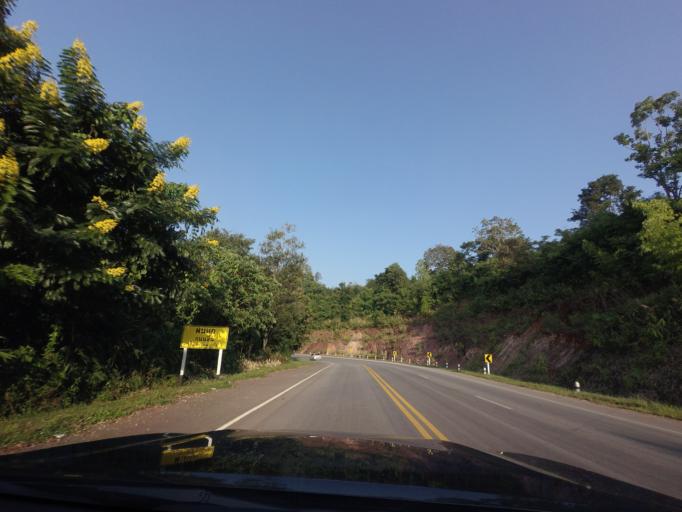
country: TH
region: Loei
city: Dan Sai
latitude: 17.2268
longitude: 101.1512
